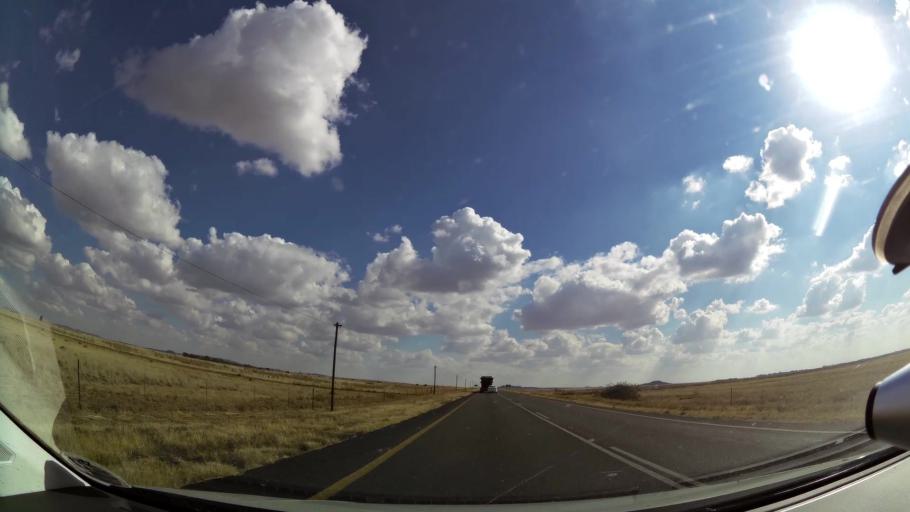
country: ZA
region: Orange Free State
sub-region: Mangaung Metropolitan Municipality
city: Bloemfontein
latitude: -29.1541
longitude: 25.7216
